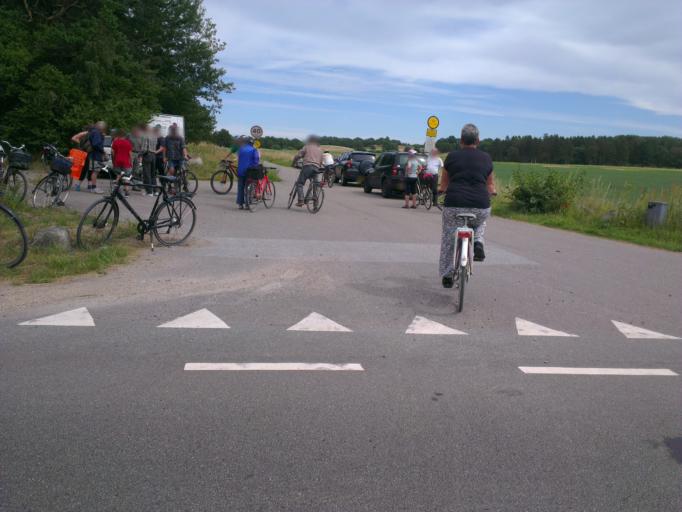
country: DK
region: Capital Region
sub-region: Frederikssund Kommune
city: Jaegerspris
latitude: 55.8922
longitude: 11.9555
